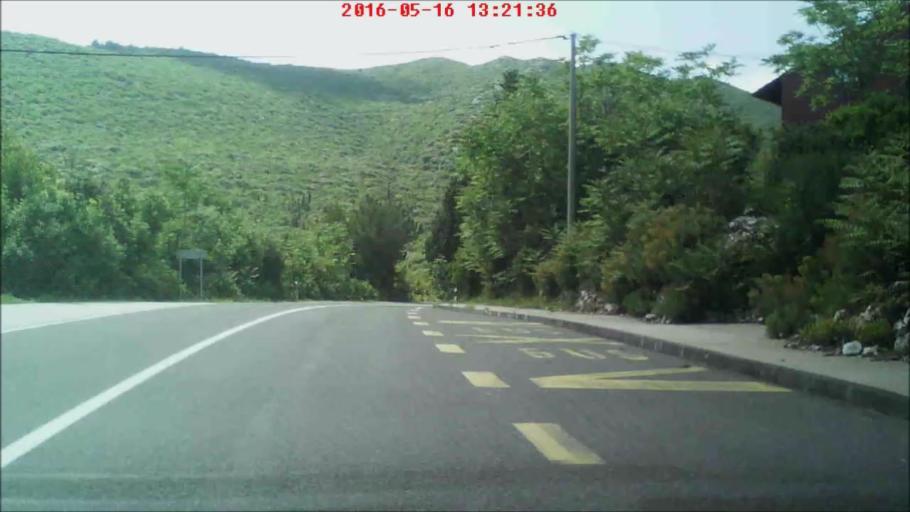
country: HR
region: Dubrovacko-Neretvanska
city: Ston
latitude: 42.8316
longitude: 17.7312
